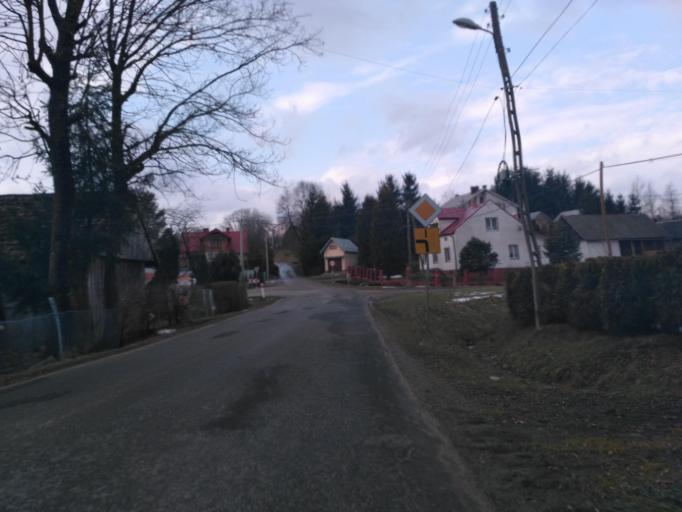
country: PL
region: Subcarpathian Voivodeship
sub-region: Powiat sanocki
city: Strachocina
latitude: 49.6087
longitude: 22.0903
